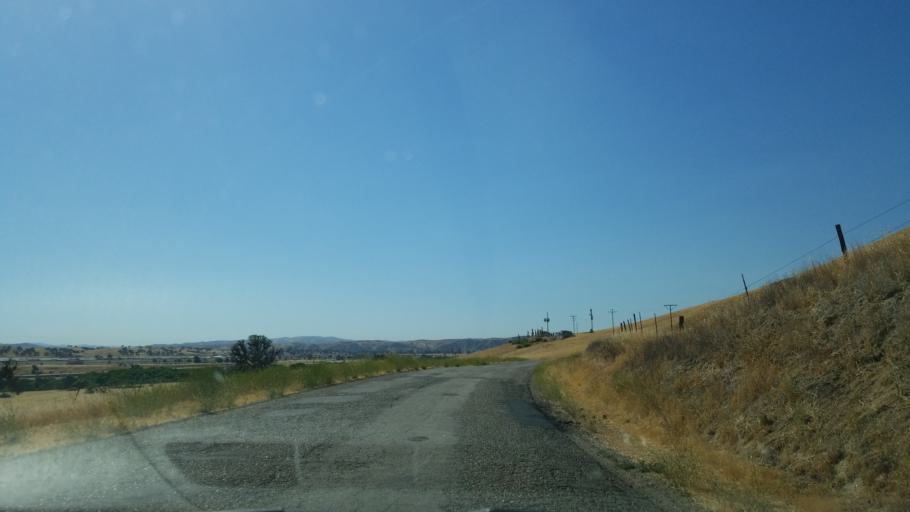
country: US
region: California
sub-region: San Luis Obispo County
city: San Miguel
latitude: 35.7887
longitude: -120.7140
